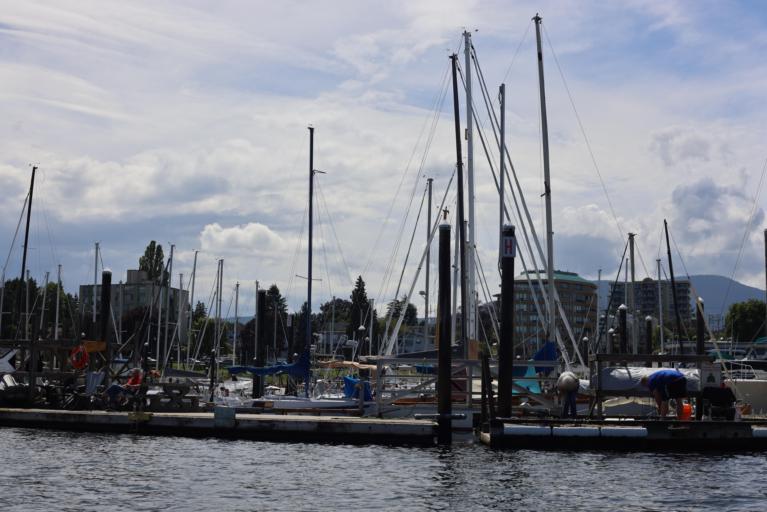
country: CA
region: British Columbia
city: Nanaimo
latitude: 49.1787
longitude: -123.9405
